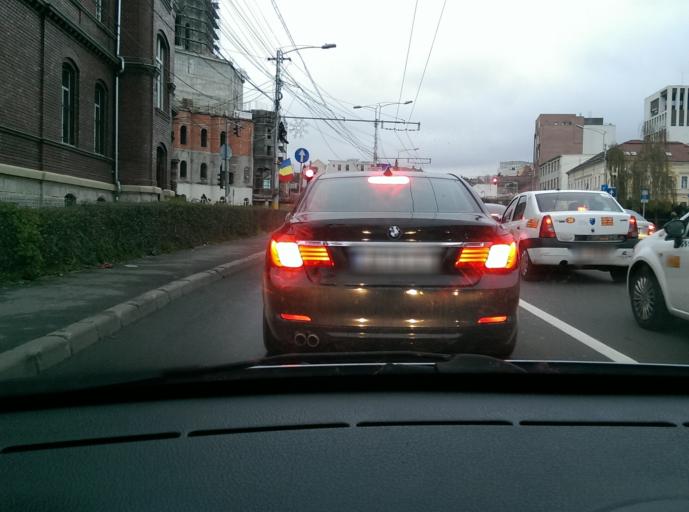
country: RO
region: Cluj
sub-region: Municipiul Cluj-Napoca
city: Cluj-Napoca
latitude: 46.7684
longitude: 23.5978
